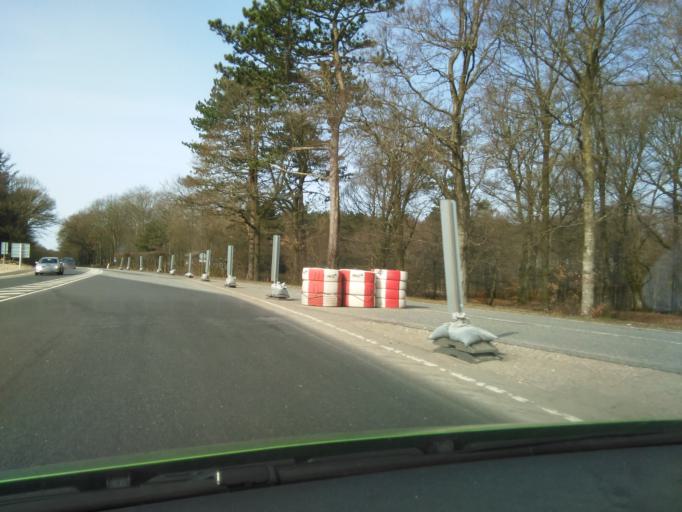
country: DK
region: Central Jutland
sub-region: Silkeborg Kommune
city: Svejbaek
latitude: 56.1570
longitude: 9.6291
